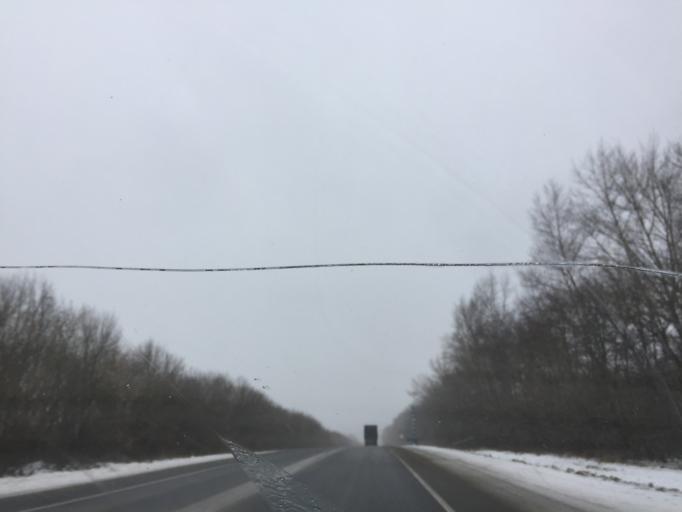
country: RU
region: Tula
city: Plavsk
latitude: 53.7616
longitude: 37.3390
